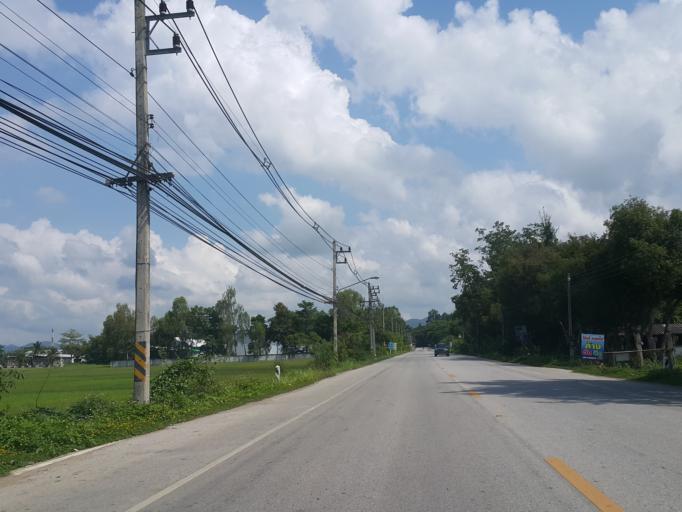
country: TH
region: Chiang Mai
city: San Sai
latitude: 18.8613
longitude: 99.1336
